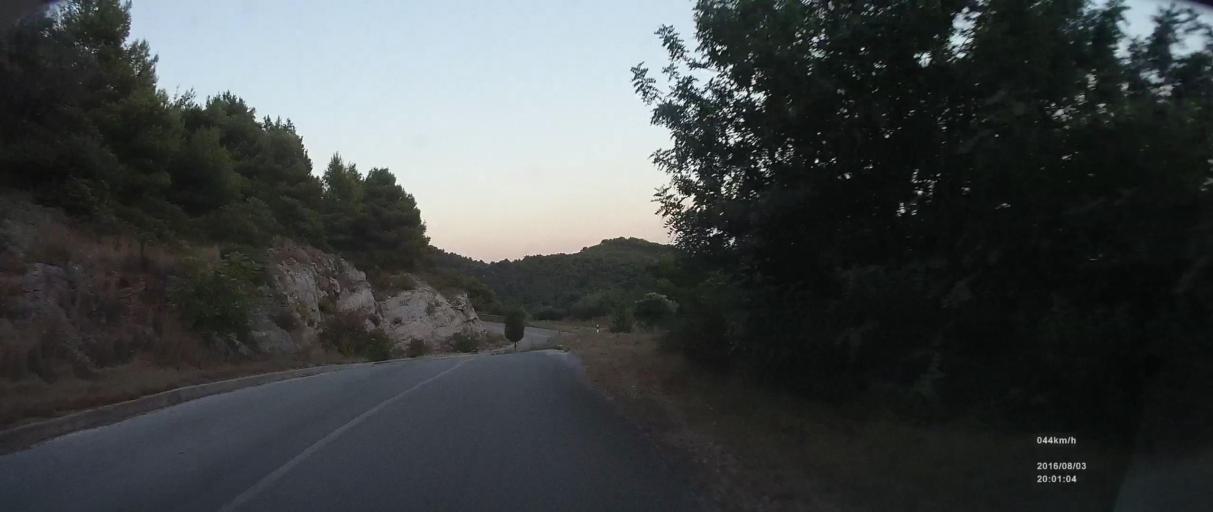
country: HR
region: Dubrovacko-Neretvanska
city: Blato
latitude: 42.7311
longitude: 17.5686
